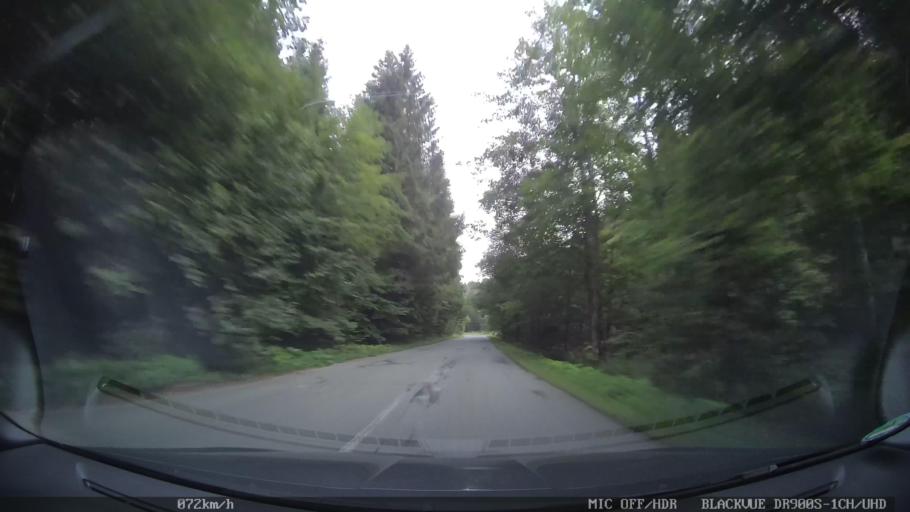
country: HR
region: Primorsko-Goranska
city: Vrbovsko
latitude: 45.2150
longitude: 15.0267
